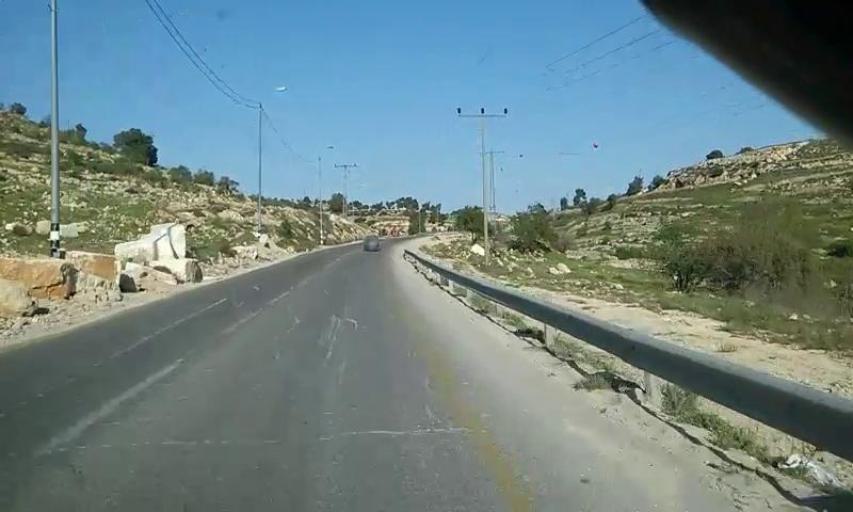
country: PS
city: Khallat ad Dar
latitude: 31.5047
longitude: 35.1276
